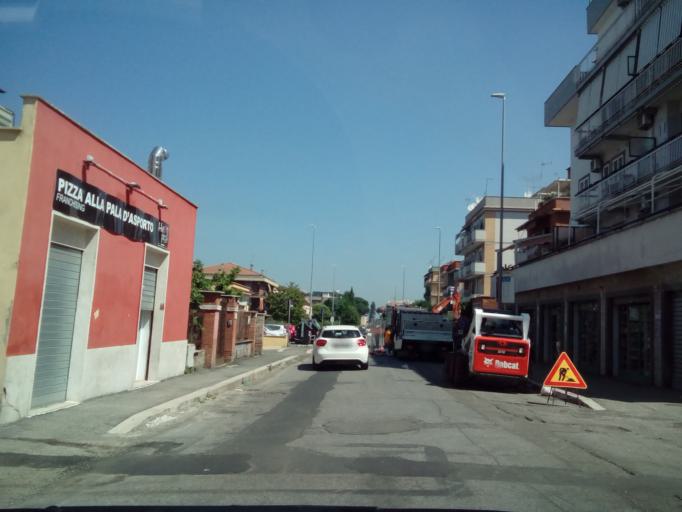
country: IT
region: Latium
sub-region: Citta metropolitana di Roma Capitale
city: Rome
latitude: 41.8827
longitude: 12.5772
